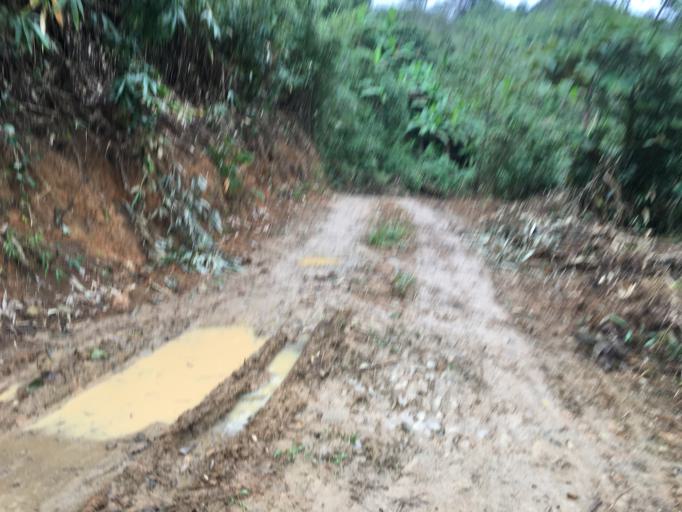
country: LA
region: Houaphan
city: Xamtay
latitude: 19.9029
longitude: 104.4594
